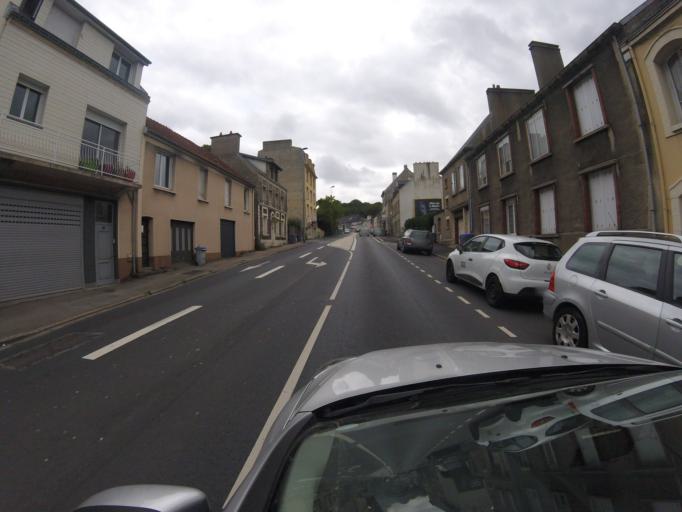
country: FR
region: Lower Normandy
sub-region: Departement de la Manche
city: Cherbourg-Octeville
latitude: 49.6252
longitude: -1.6168
